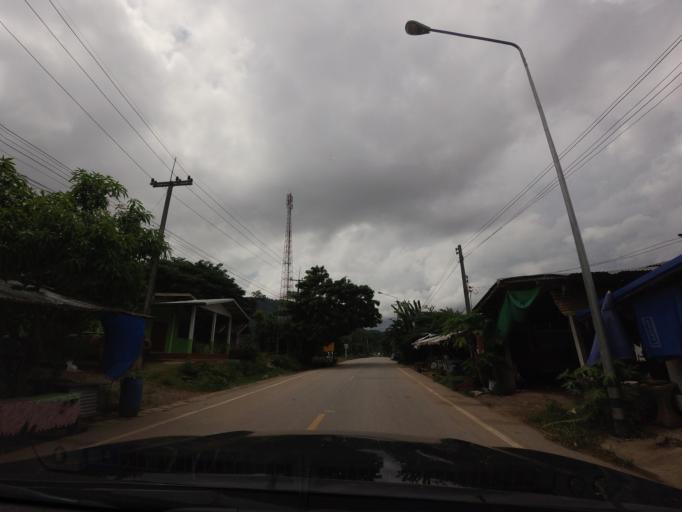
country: TH
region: Loei
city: Pak Chom
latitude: 18.0574
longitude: 101.8027
